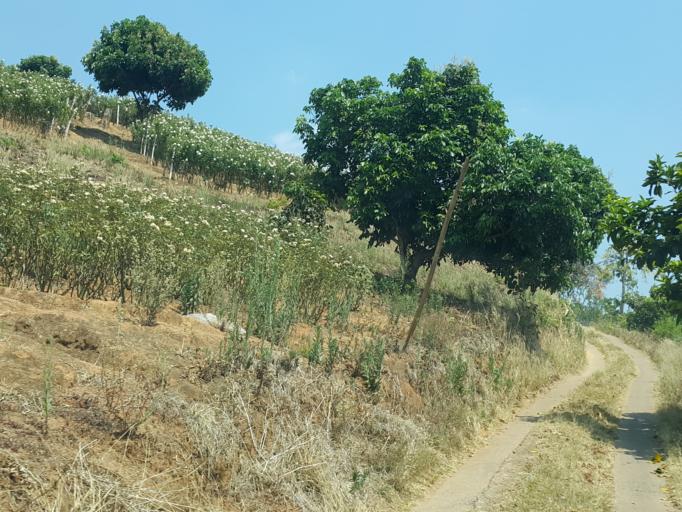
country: TH
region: Chiang Mai
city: Samoeng
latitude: 18.8919
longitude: 98.7743
